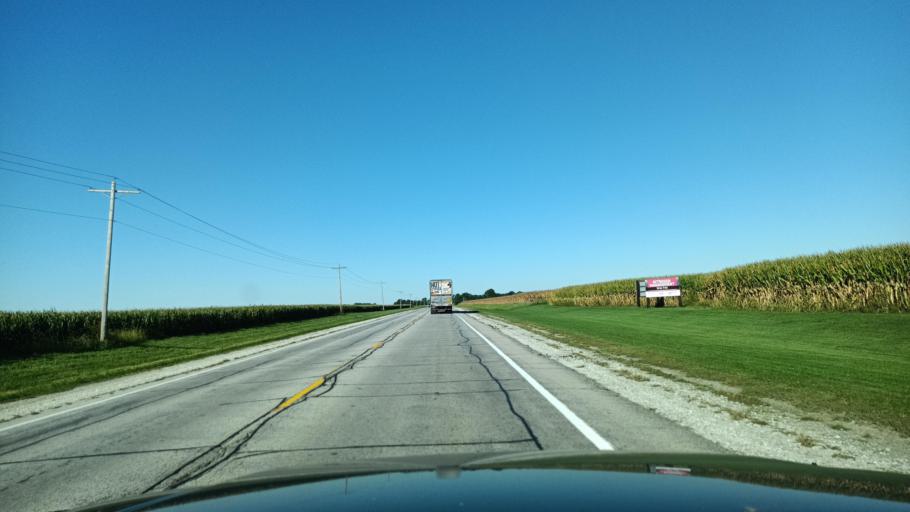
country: US
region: Illinois
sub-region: Warren County
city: Monmouth
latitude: 40.8783
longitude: -90.6947
